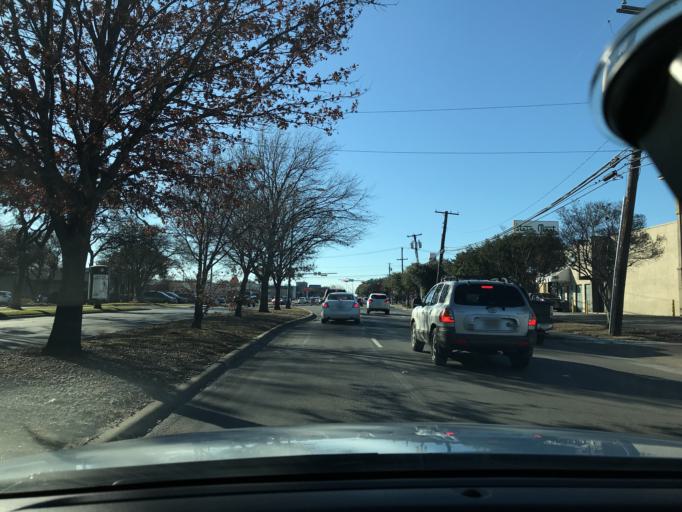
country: US
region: Texas
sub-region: Dallas County
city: Highland Park
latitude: 32.8365
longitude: -96.7513
